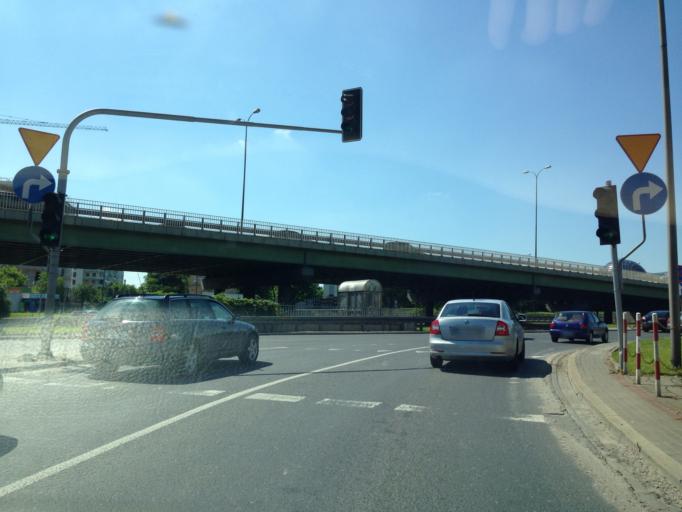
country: PL
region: Masovian Voivodeship
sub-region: Warszawa
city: Ochota
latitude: 52.2167
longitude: 20.9602
